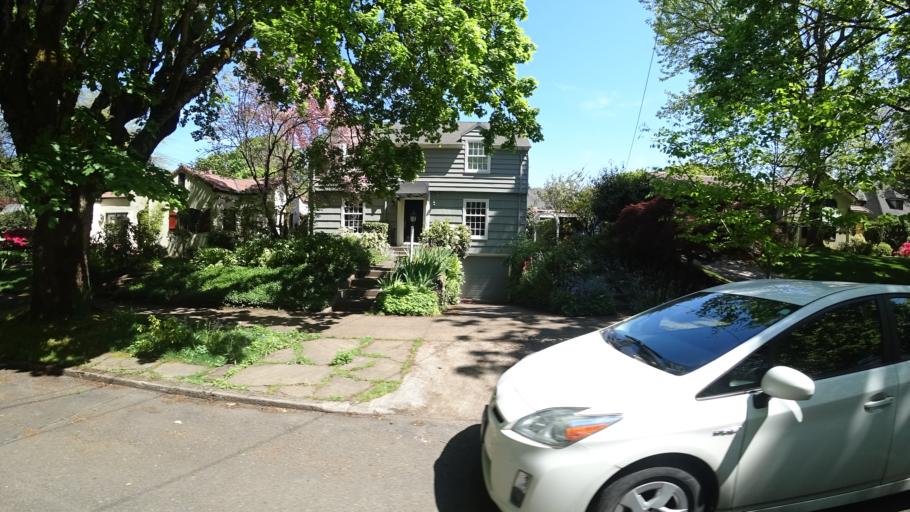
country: US
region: Oregon
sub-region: Clackamas County
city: Milwaukie
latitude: 45.4707
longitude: -122.6282
